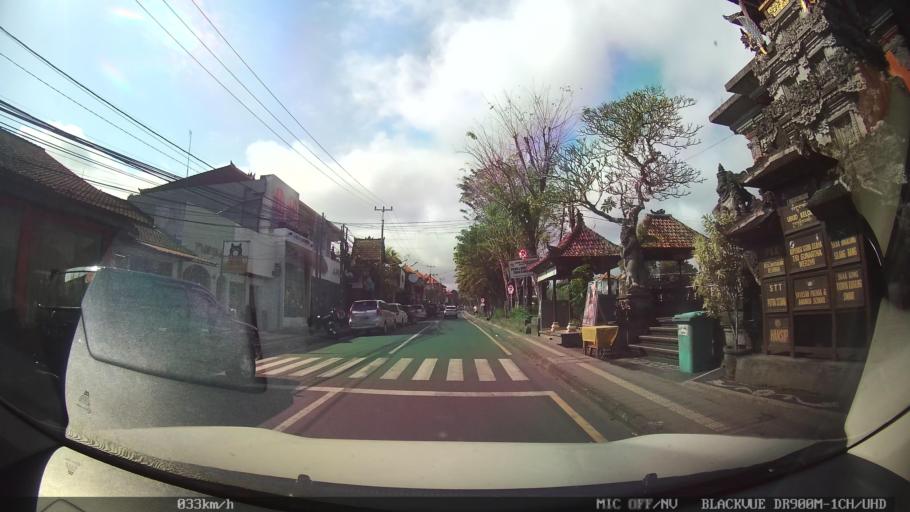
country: ID
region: Bali
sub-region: Kabupaten Gianyar
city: Ubud
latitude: -8.5111
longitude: 115.2615
